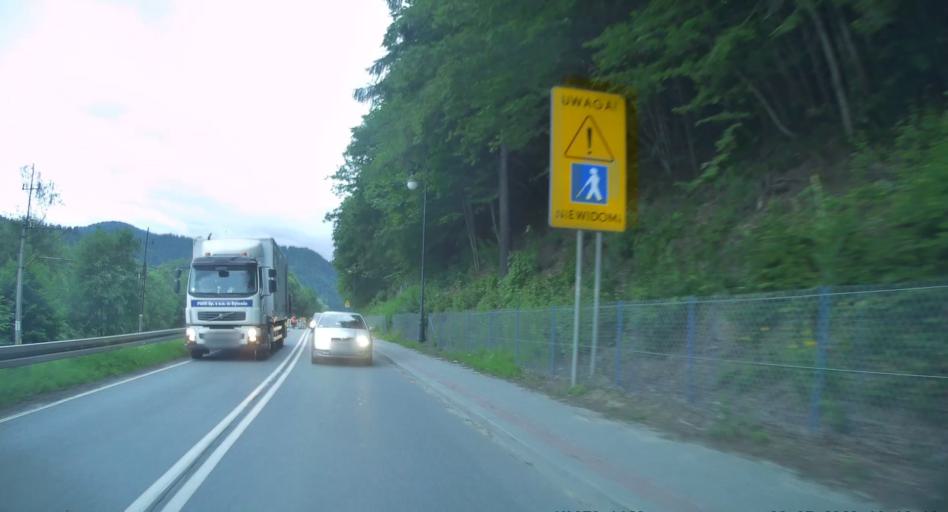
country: PL
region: Lesser Poland Voivodeship
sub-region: Powiat nowosadecki
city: Muszyna
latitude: 49.3508
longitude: 20.8845
